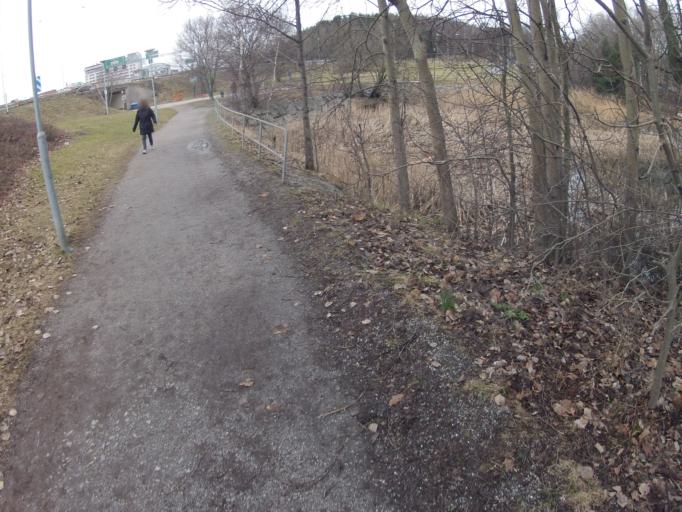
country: SE
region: Stockholm
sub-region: Norrtalje Kommun
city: Bergshamra
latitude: 59.3775
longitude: 18.0149
